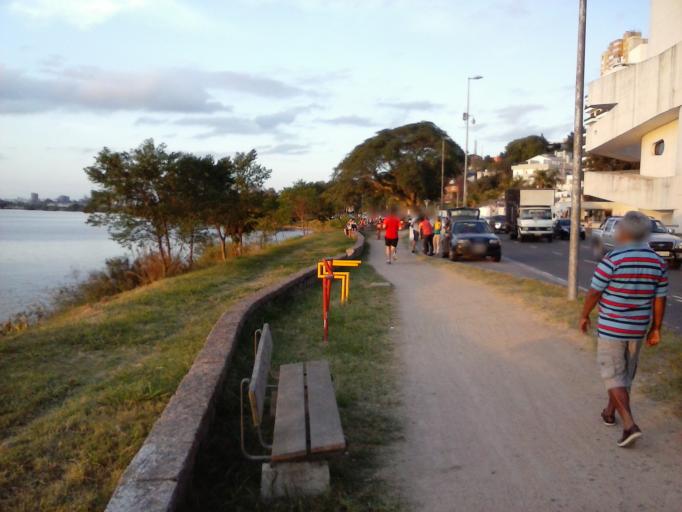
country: BR
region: Rio Grande do Sul
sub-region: Porto Alegre
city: Porto Alegre
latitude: -30.0779
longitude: -51.2464
